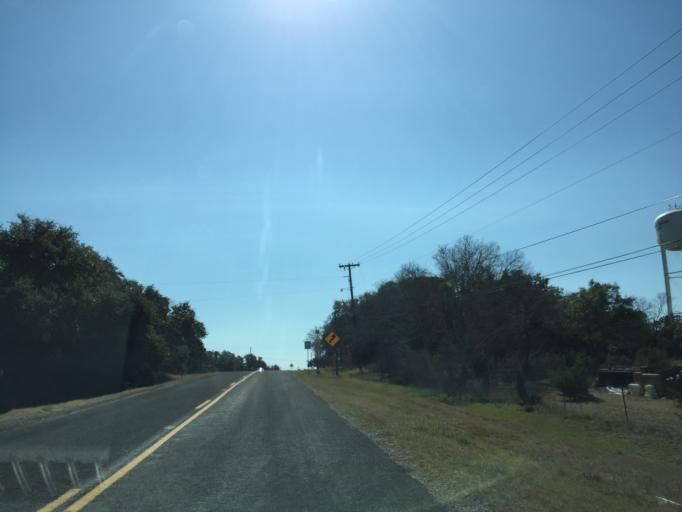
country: US
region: Texas
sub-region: Williamson County
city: Serenada
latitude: 30.7460
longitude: -97.5999
